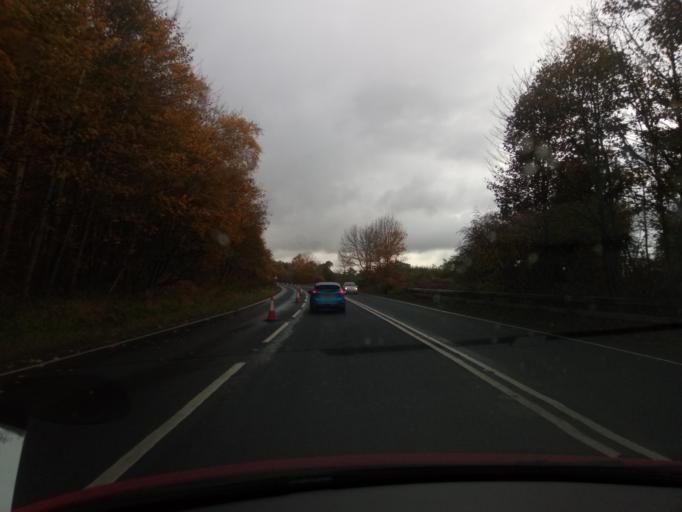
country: GB
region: England
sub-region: Northumberland
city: Healey
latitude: 54.9457
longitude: -1.9642
